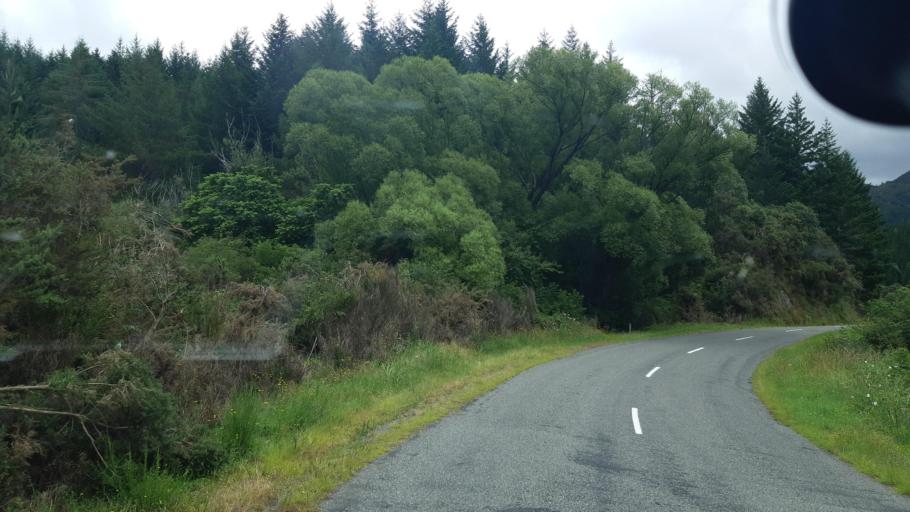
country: NZ
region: Marlborough
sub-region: Marlborough District
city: Blenheim
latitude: -41.4521
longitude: 173.7214
